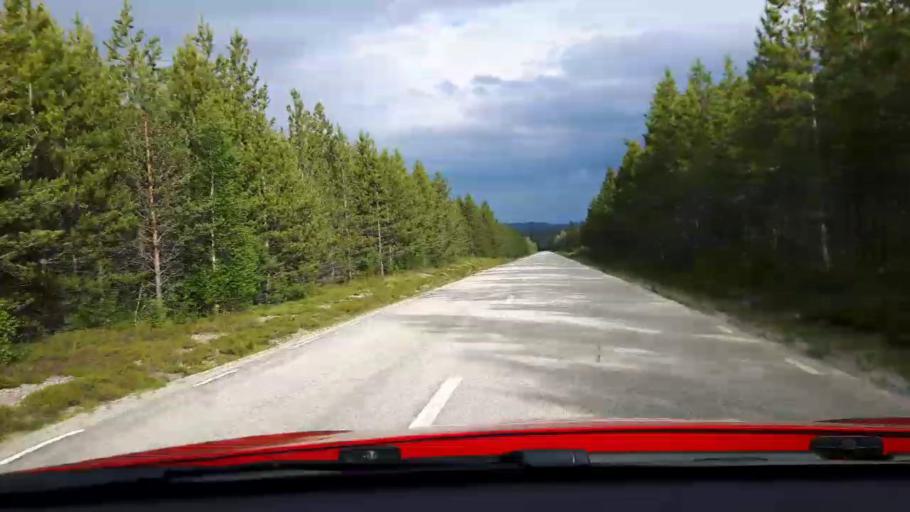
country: SE
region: Jaemtland
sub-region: Bergs Kommun
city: Hoverberg
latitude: 62.6704
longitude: 14.0302
